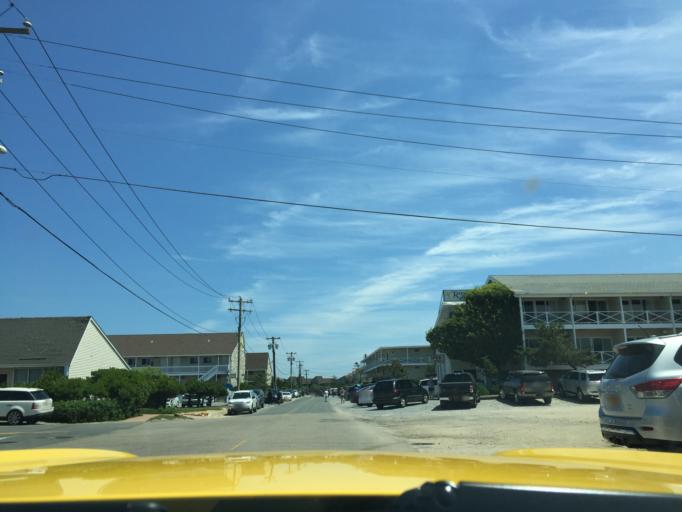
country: US
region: New York
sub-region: Suffolk County
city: Montauk
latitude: 41.0328
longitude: -71.9437
